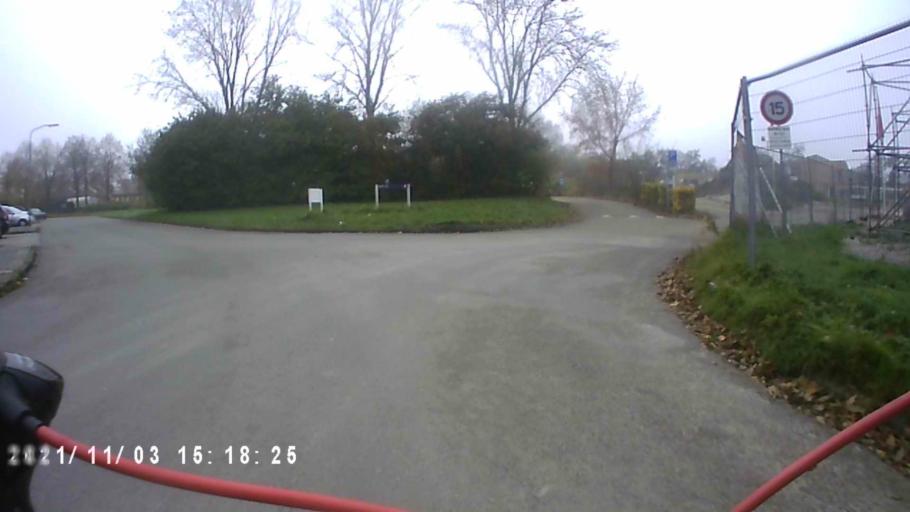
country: NL
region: Groningen
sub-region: Gemeente Leek
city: Leek
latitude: 53.1620
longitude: 6.3624
